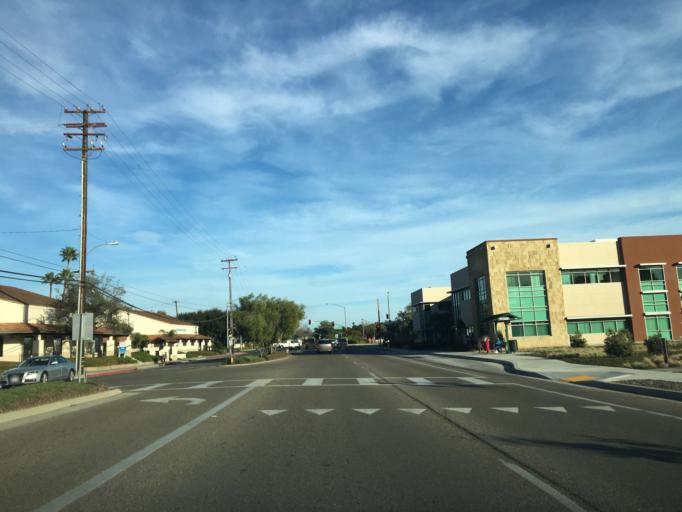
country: US
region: California
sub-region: Santa Barbara County
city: Goleta
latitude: 34.4350
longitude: -119.8108
